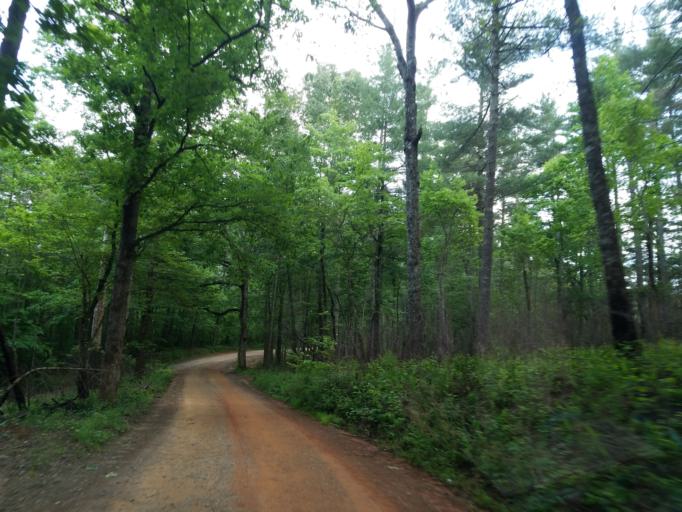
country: US
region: Georgia
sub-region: Lumpkin County
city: Dahlonega
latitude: 34.5852
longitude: -84.1250
